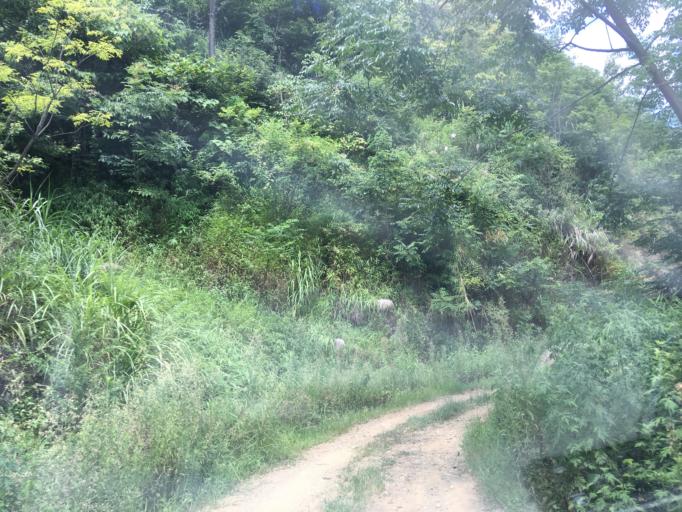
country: CN
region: Guangxi Zhuangzu Zizhiqu
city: Tongle
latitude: 24.9714
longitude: 105.9737
